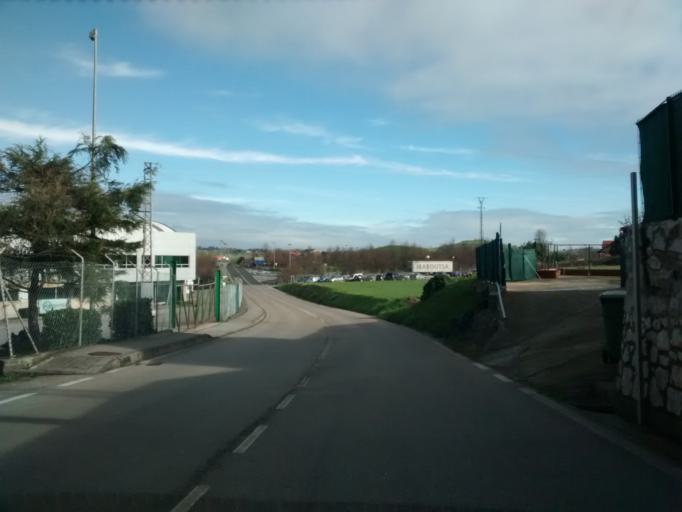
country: ES
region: Cantabria
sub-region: Provincia de Cantabria
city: Lierganes
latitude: 43.3977
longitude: -3.7656
